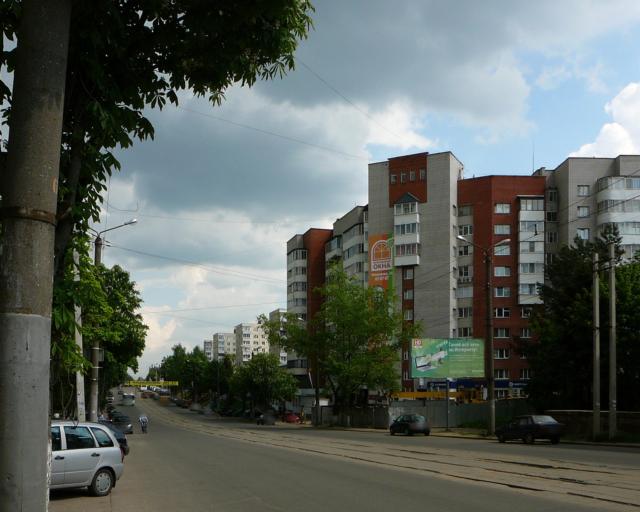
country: RU
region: Smolensk
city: Smolensk
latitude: 54.7722
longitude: 32.0314
